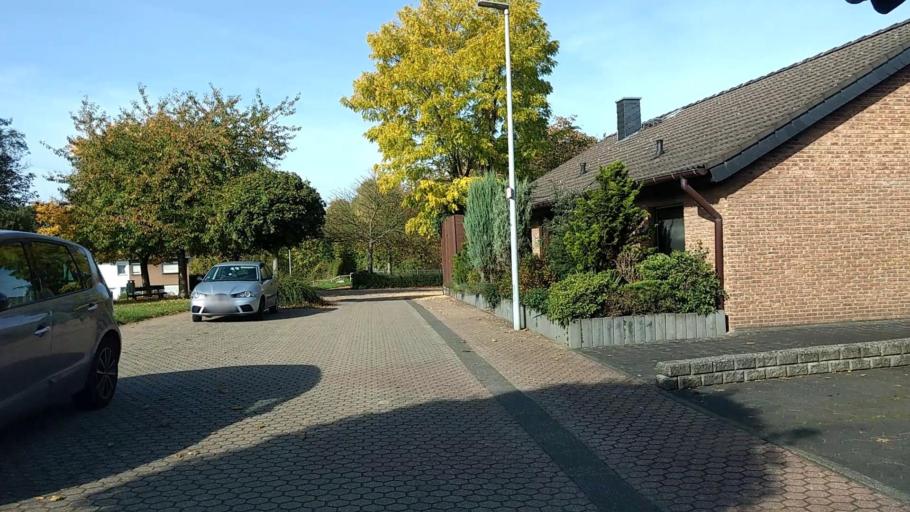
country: DE
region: North Rhine-Westphalia
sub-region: Regierungsbezirk Koln
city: Bergheim
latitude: 50.9360
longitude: 6.6911
